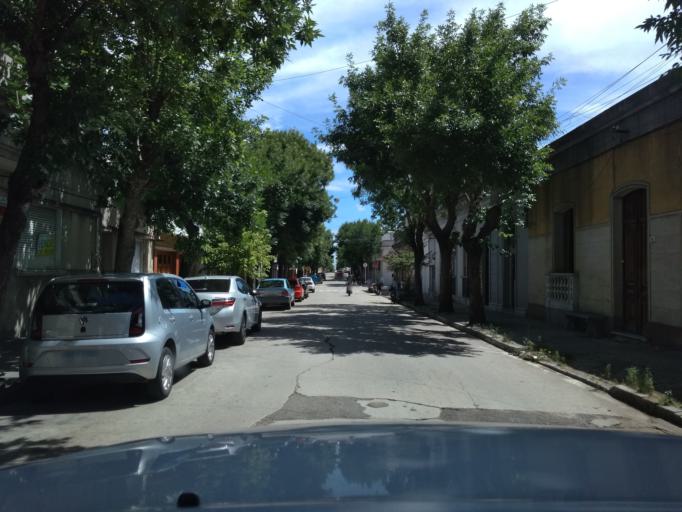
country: UY
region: Florida
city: Florida
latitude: -34.0999
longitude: -56.2128
